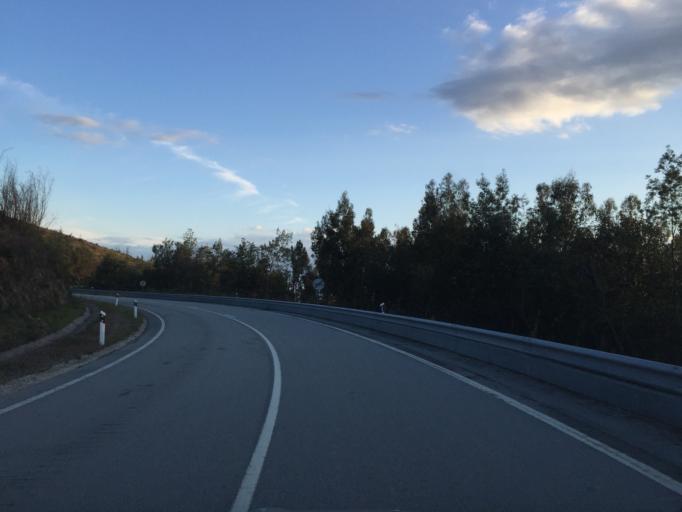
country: PT
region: Coimbra
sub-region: Pampilhosa da Serra
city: Pampilhosa da Serra
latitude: 40.0911
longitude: -7.9912
